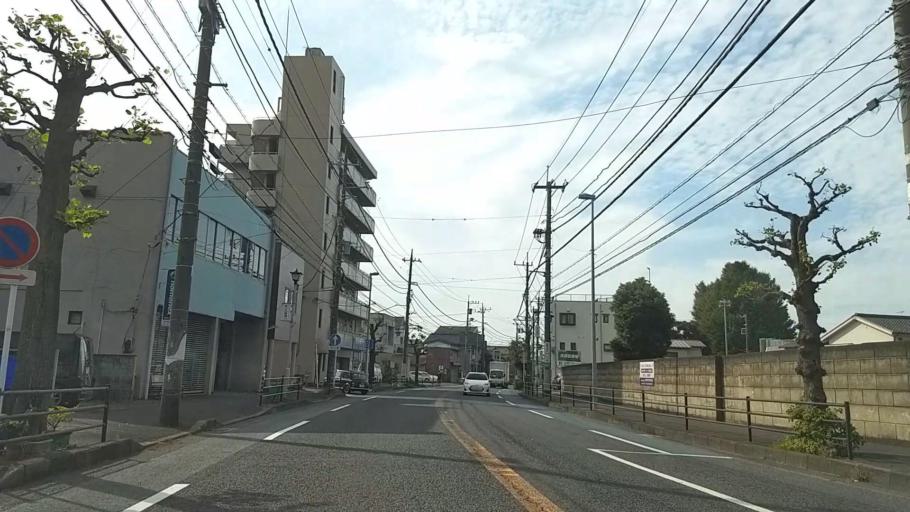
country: JP
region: Kanagawa
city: Atsugi
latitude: 35.4377
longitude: 139.3700
